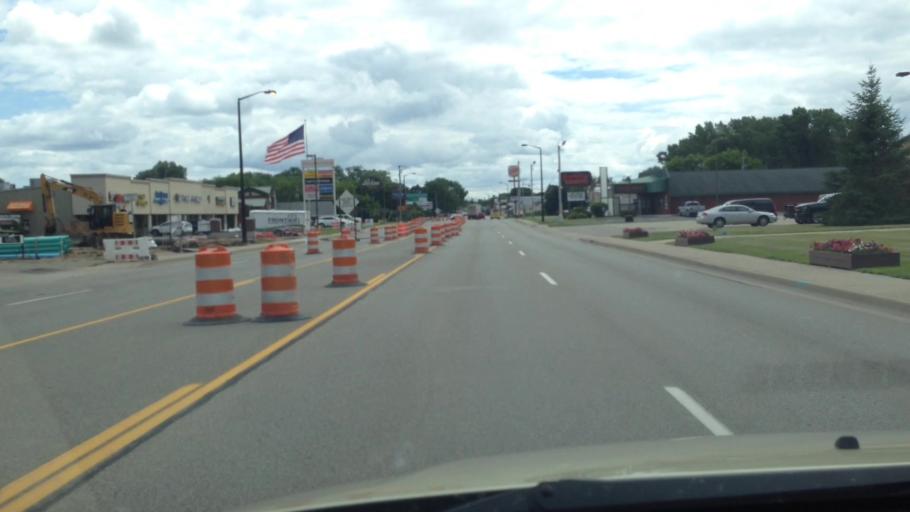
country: US
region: Michigan
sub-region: Menominee County
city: Menominee
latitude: 45.1213
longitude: -87.6134
